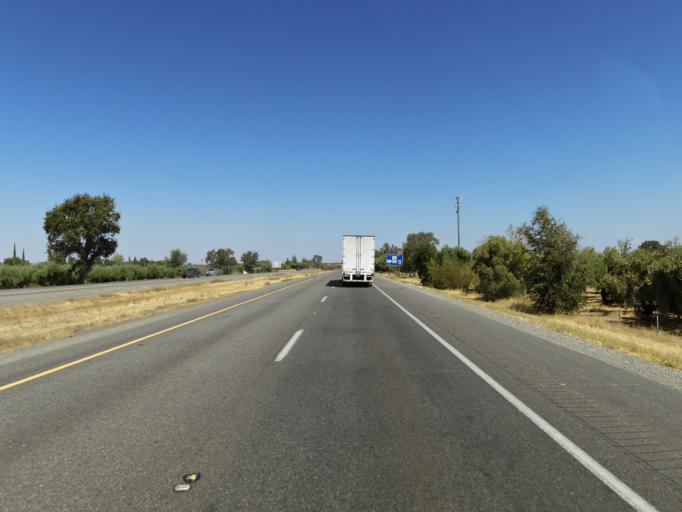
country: US
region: California
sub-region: Tehama County
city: Corning
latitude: 39.9215
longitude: -122.2001
